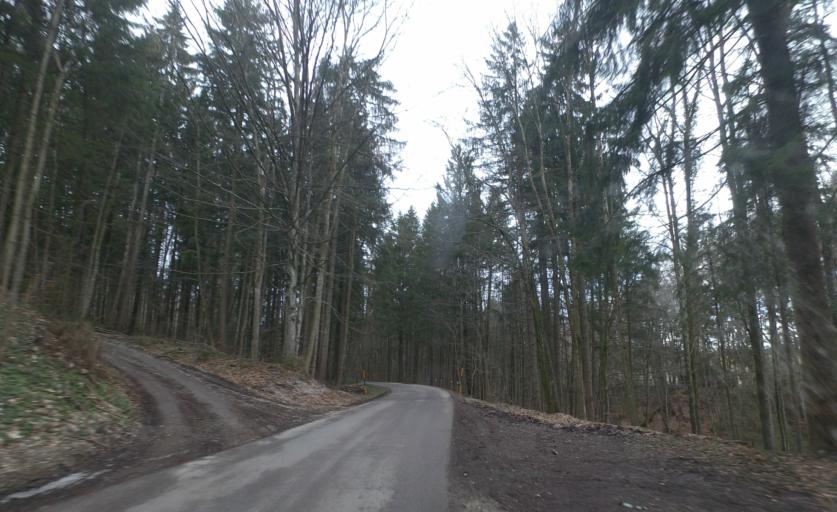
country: DE
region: Bavaria
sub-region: Upper Bavaria
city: Teisendorf
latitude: 47.8245
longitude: 12.7655
